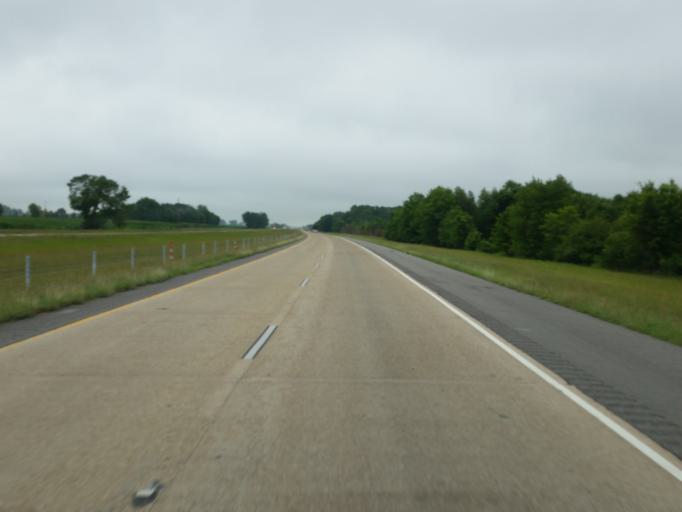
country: US
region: Louisiana
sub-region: Madison Parish
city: Tallulah
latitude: 32.3354
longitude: -91.0582
